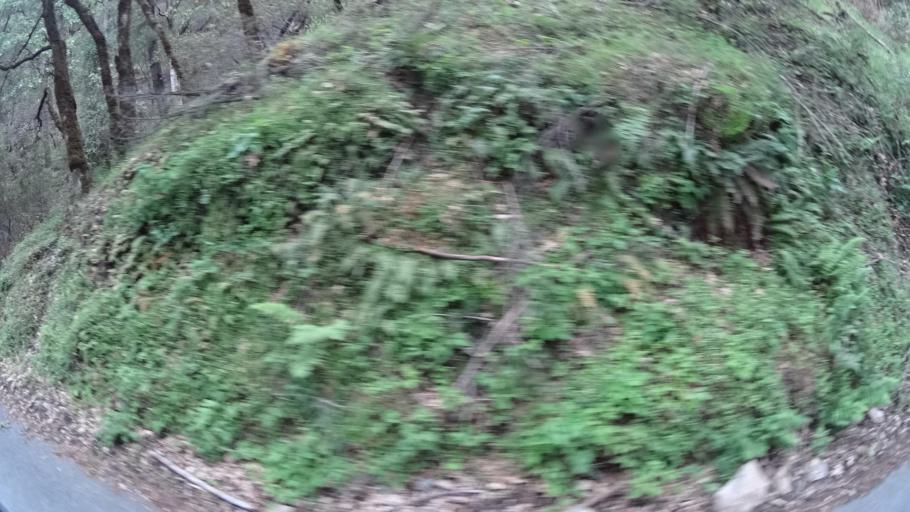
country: US
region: California
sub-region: Humboldt County
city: Willow Creek
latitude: 40.9332
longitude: -123.6152
